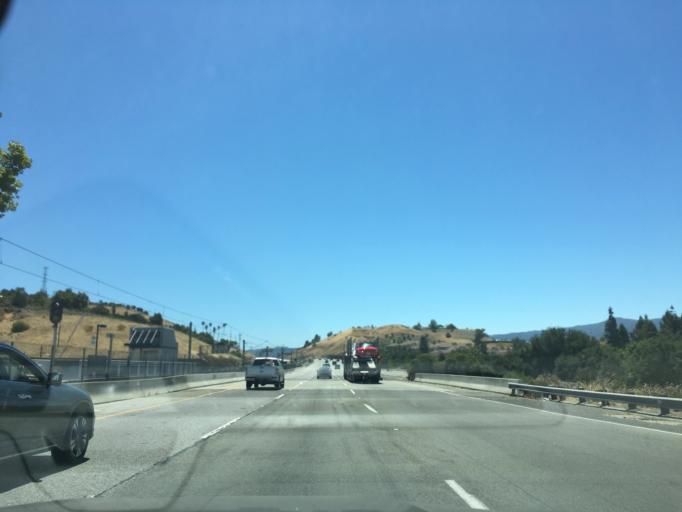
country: US
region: California
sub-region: Santa Clara County
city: Seven Trees
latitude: 37.2933
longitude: -121.8727
